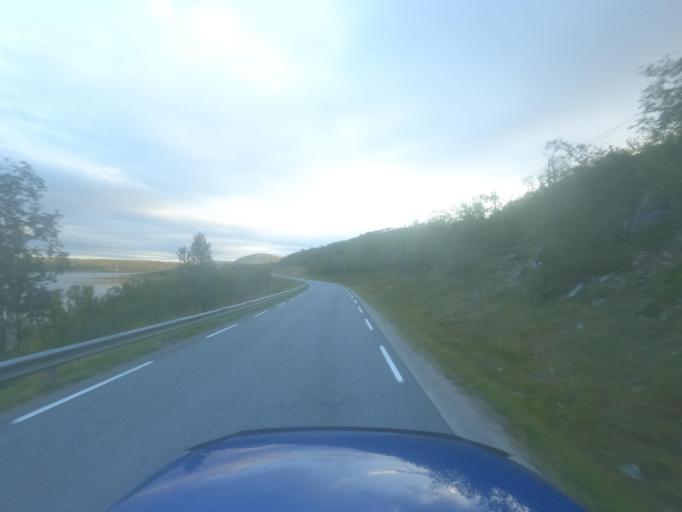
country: NO
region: Finnmark Fylke
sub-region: Porsanger
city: Lakselv
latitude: 70.3376
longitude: 25.0720
